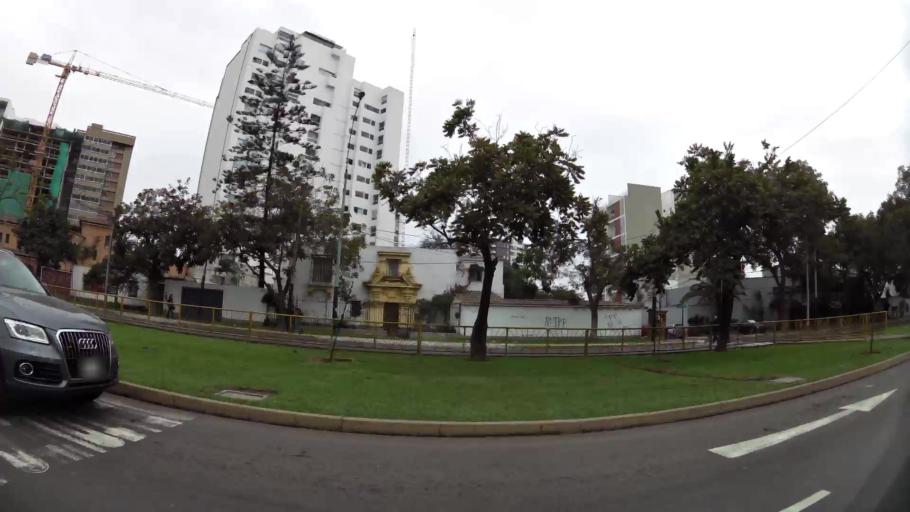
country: PE
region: Lima
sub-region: Lima
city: San Isidro
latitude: -12.0939
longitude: -77.0518
